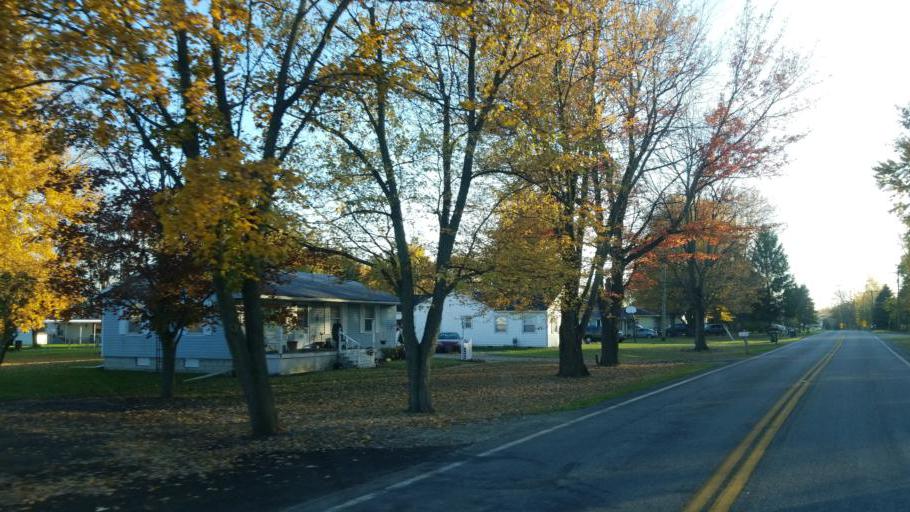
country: US
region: Ohio
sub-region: Sandusky County
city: Green Springs
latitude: 41.3277
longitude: -83.0522
